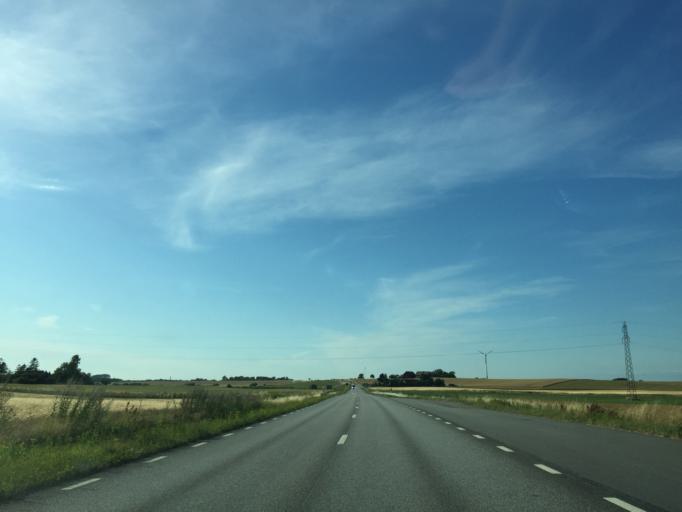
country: SE
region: Skane
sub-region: Svedala Kommun
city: Klagerup
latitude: 55.6137
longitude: 13.2637
